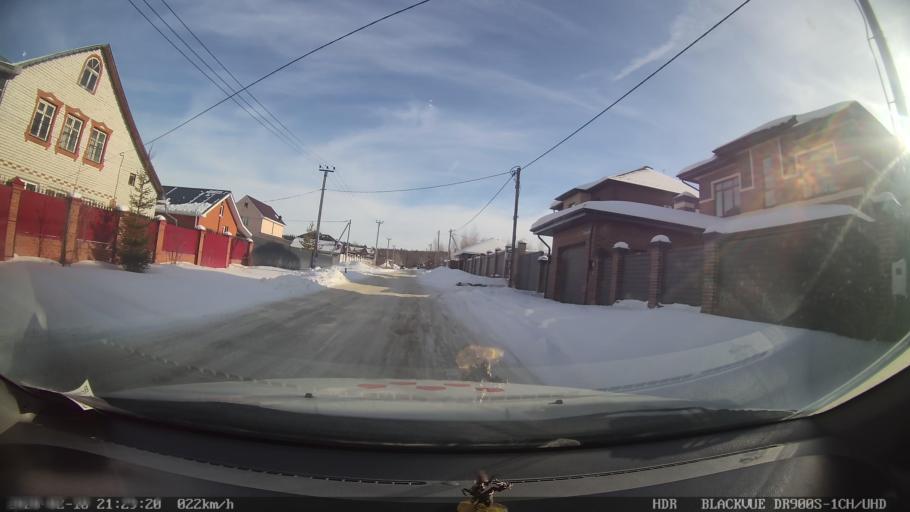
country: RU
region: Tatarstan
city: Vysokaya Gora
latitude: 55.7796
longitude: 49.2710
